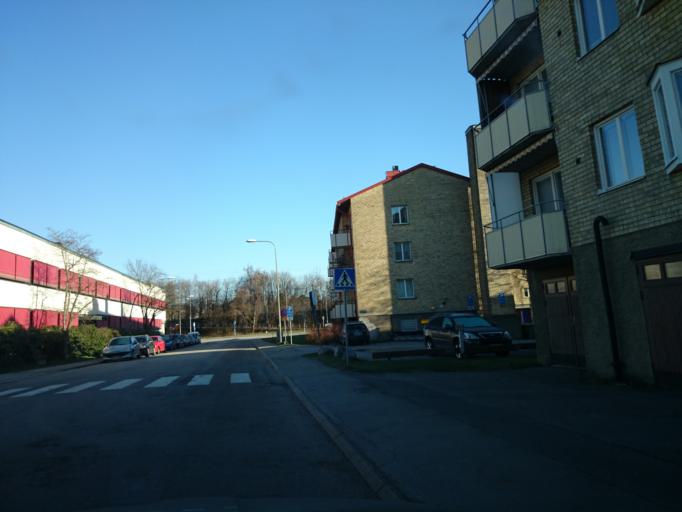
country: SE
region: Stockholm
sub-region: Huddinge Kommun
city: Segeltorp
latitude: 59.2878
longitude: 17.9658
